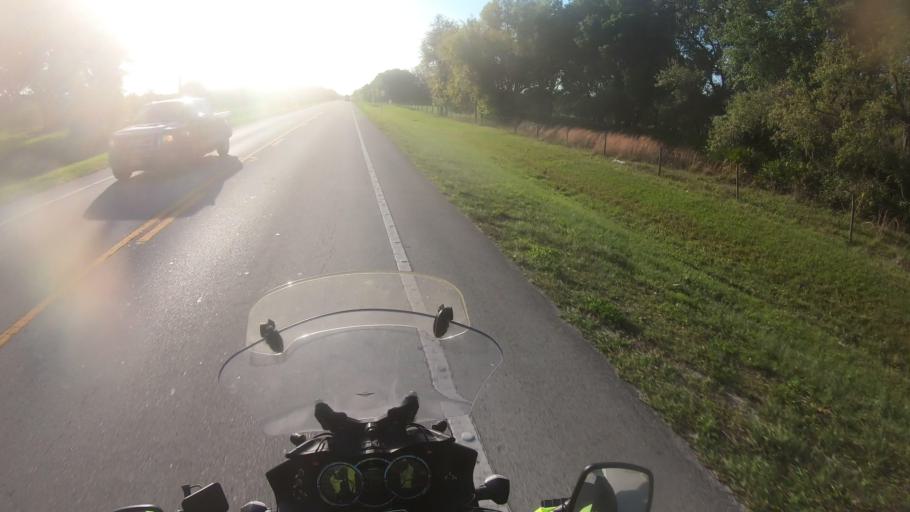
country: US
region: Florida
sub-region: DeSoto County
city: Arcadia
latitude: 27.2304
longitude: -81.9005
